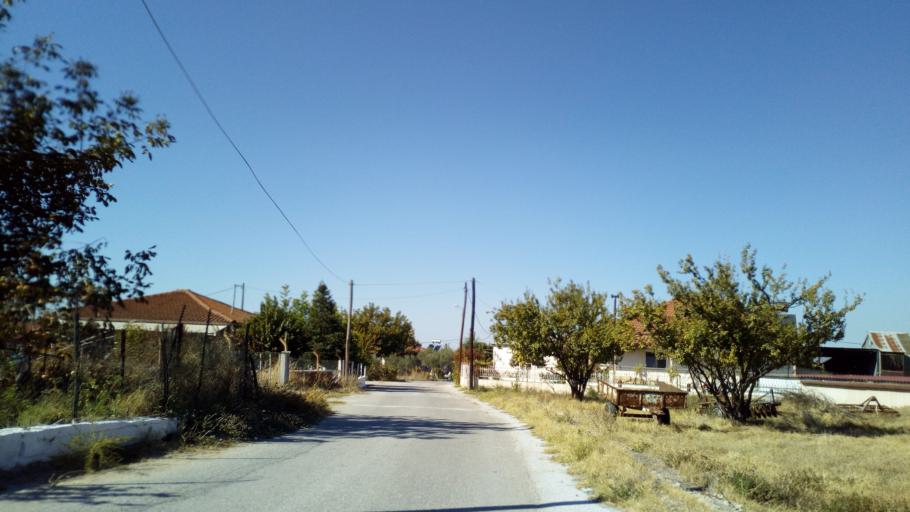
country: GR
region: Central Macedonia
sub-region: Nomos Thessalonikis
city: Gerakarou
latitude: 40.6361
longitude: 23.2511
